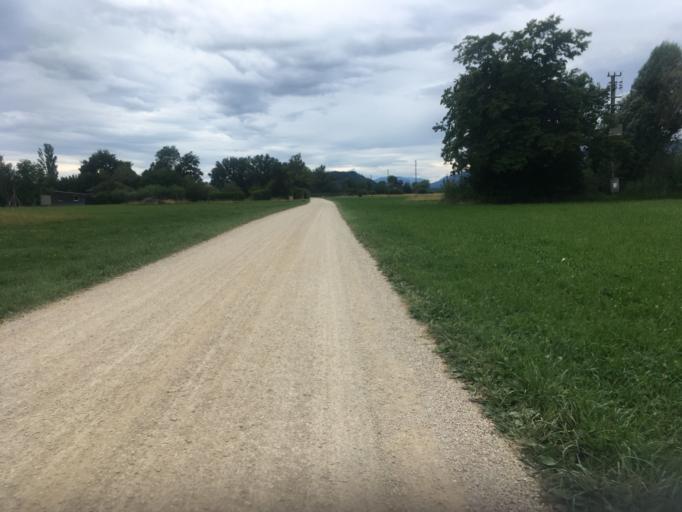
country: CH
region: Bern
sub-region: Jura bernois
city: La Neuveville
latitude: 47.0587
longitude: 7.1278
